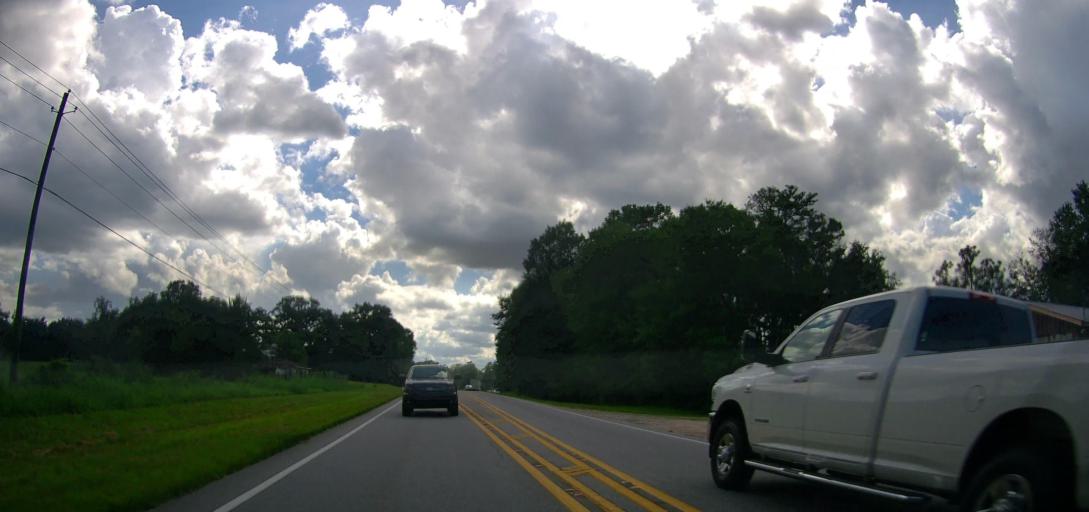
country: US
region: Alabama
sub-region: Russell County
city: Ladonia
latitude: 32.4576
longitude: -85.1838
